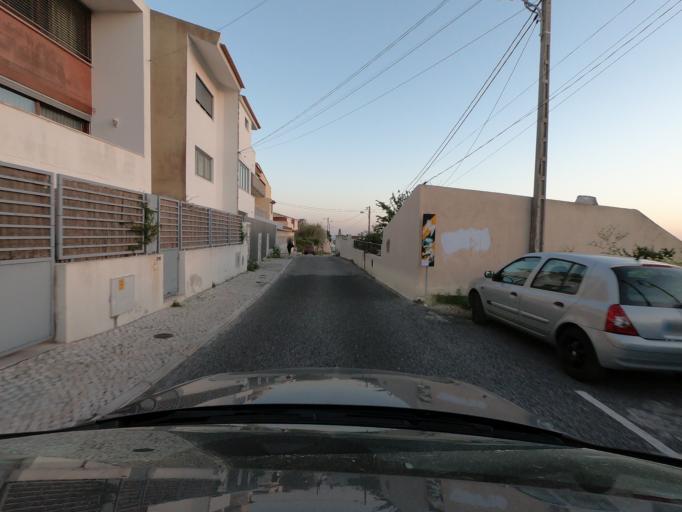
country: PT
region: Lisbon
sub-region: Cascais
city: Sao Domingos de Rana
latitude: 38.7017
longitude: -9.3308
